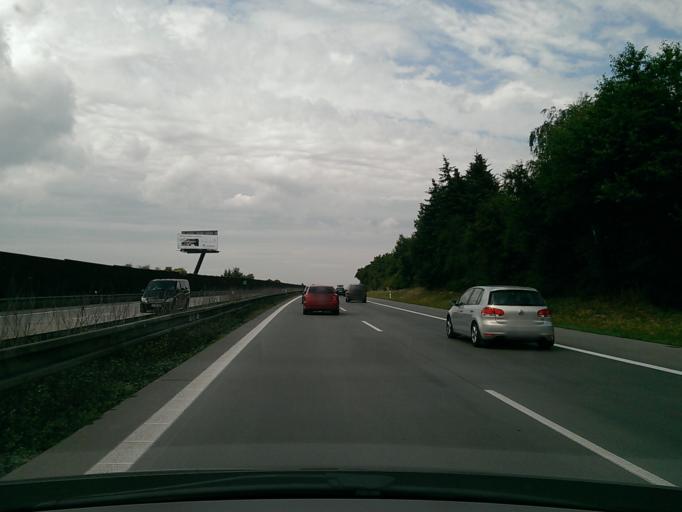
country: CZ
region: Vysocina
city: Merin
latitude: 49.3912
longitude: 15.9032
